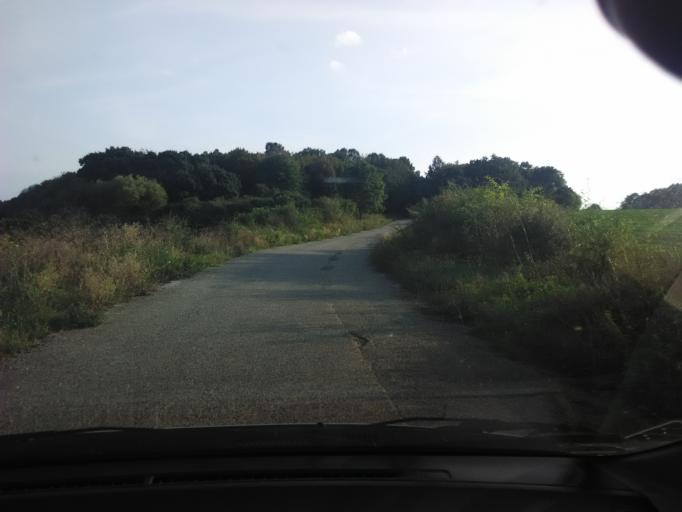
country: SK
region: Nitriansky
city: Levice
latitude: 48.2941
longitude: 18.7018
